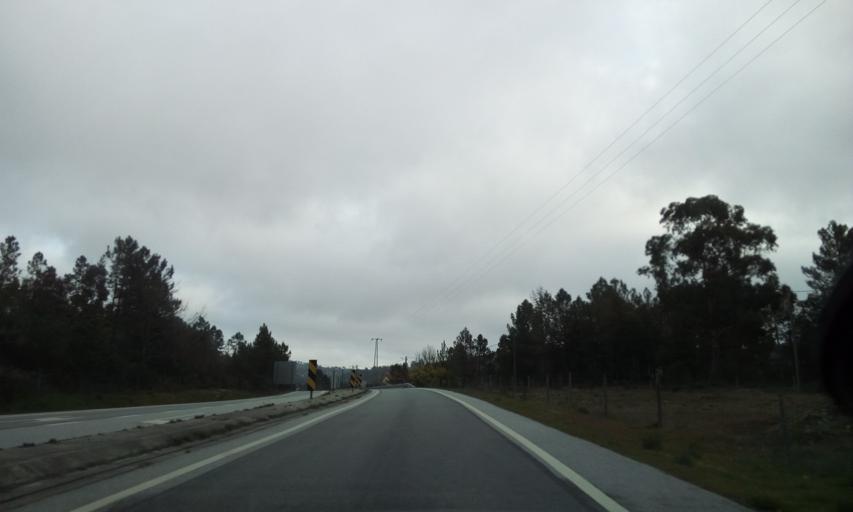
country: PT
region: Guarda
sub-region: Fornos de Algodres
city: Fornos de Algodres
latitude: 40.6380
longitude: -7.4961
